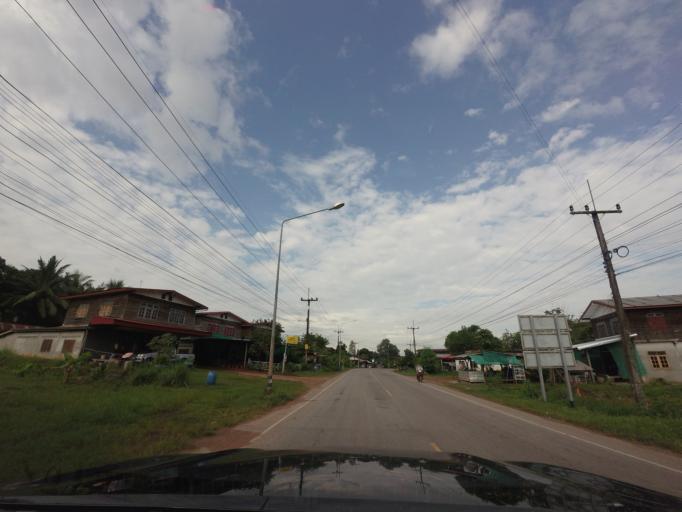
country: TH
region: Nong Khai
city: Pho Tak
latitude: 17.7800
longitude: 102.3828
